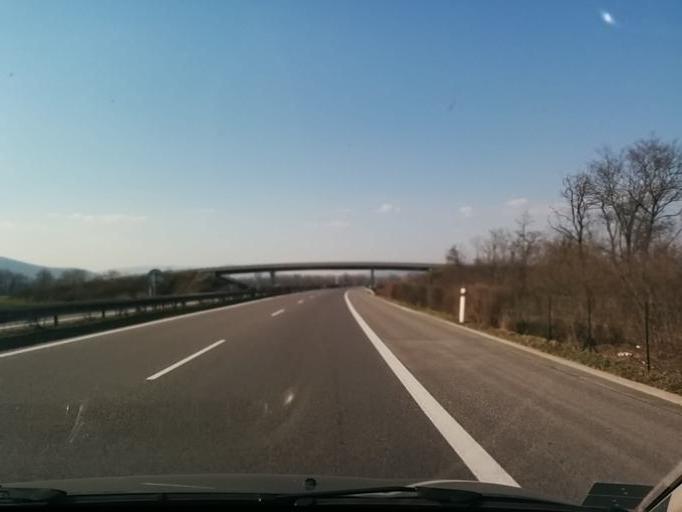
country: SK
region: Trenciansky
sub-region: Okres Nove Mesto nad Vahom
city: Nove Mesto nad Vahom
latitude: 48.7360
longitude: 17.8642
